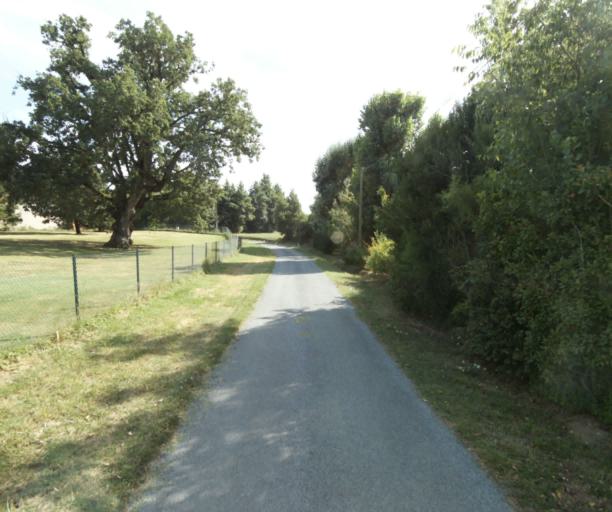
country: FR
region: Midi-Pyrenees
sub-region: Departement du Tarn
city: Puylaurens
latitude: 43.5242
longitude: 2.0450
